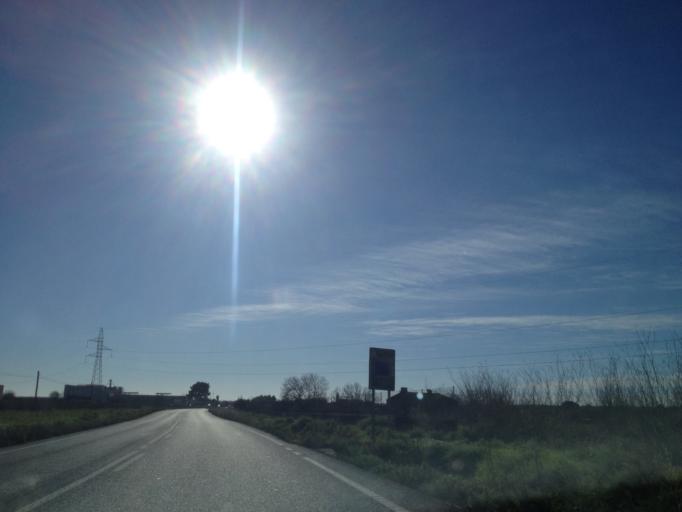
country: ES
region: Balearic Islands
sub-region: Illes Balears
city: Petra
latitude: 39.6305
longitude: 3.1064
